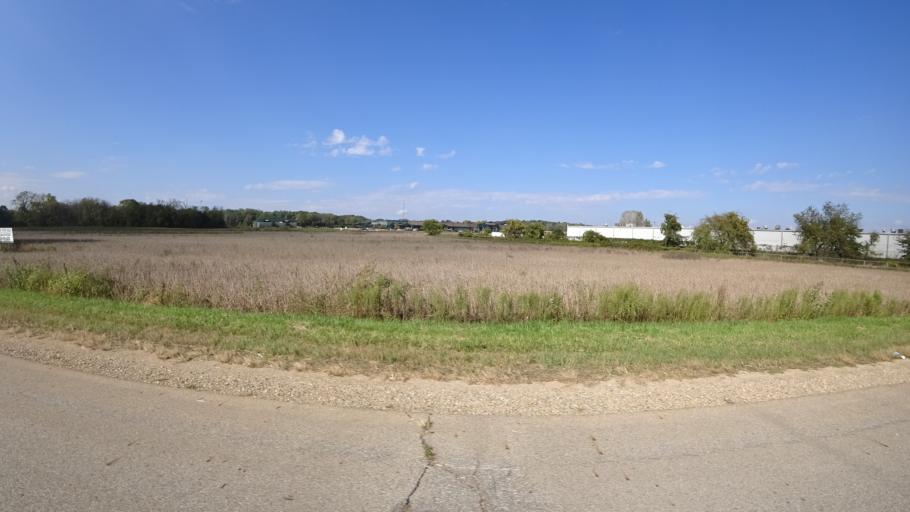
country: US
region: Michigan
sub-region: Saint Joseph County
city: Three Rivers
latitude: 41.9289
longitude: -85.6529
